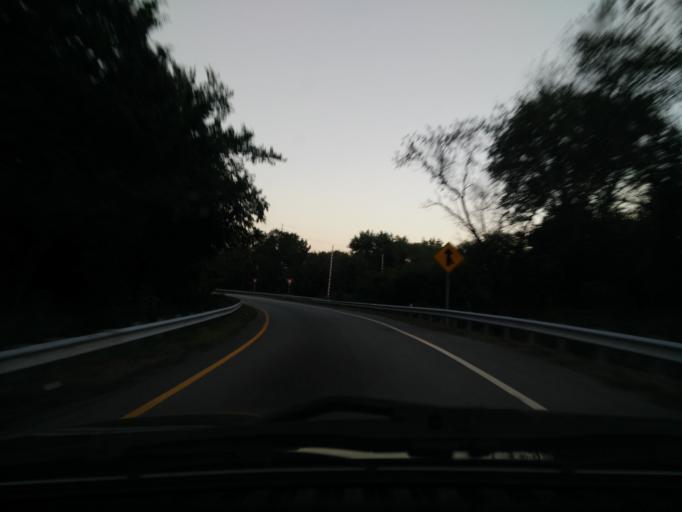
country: US
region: Virginia
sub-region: City of Chesapeake
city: Chesapeake
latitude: 36.8440
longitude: -76.1987
